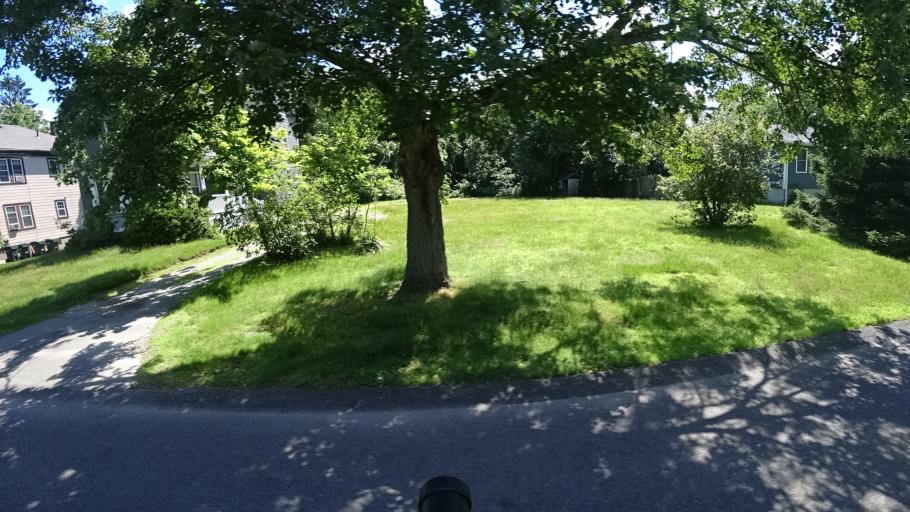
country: US
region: Massachusetts
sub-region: Norfolk County
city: Dedham
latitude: 42.2558
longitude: -71.1514
